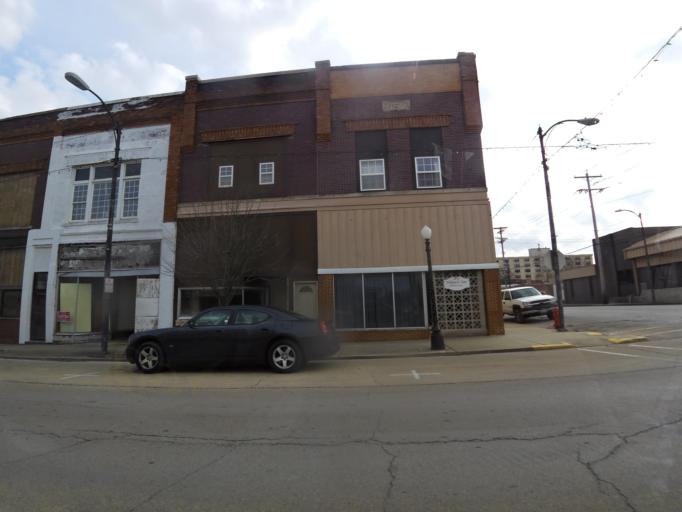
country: US
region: Illinois
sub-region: Christian County
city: Pana
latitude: 39.3880
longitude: -89.0821
